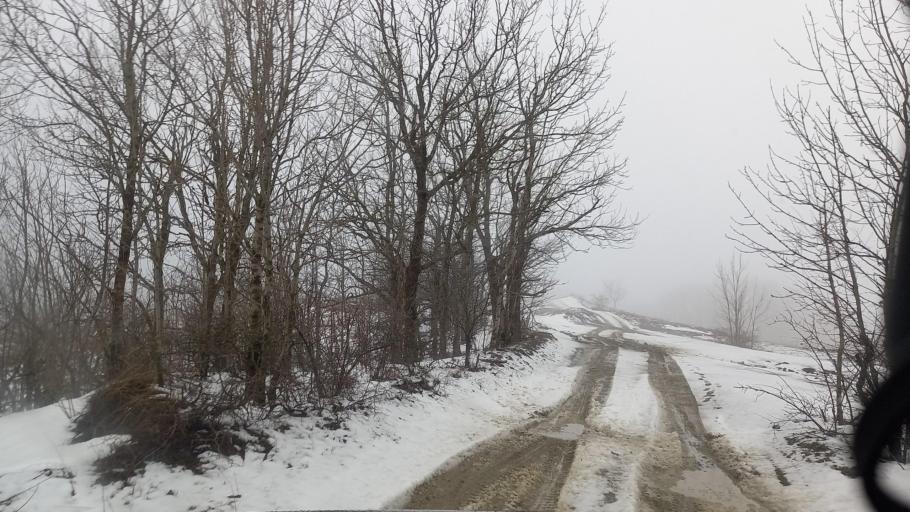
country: RU
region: Krasnodarskiy
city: Divnomorskoye
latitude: 44.6065
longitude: 38.2477
